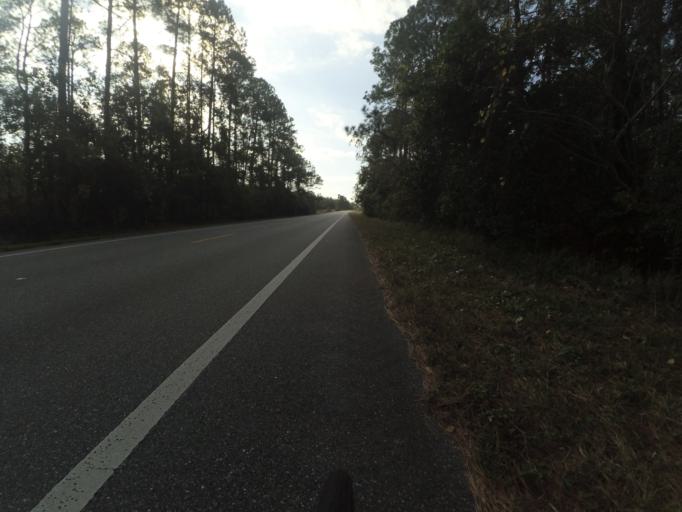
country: US
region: Florida
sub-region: Lake County
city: Astor
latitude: 29.1141
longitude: -81.6176
